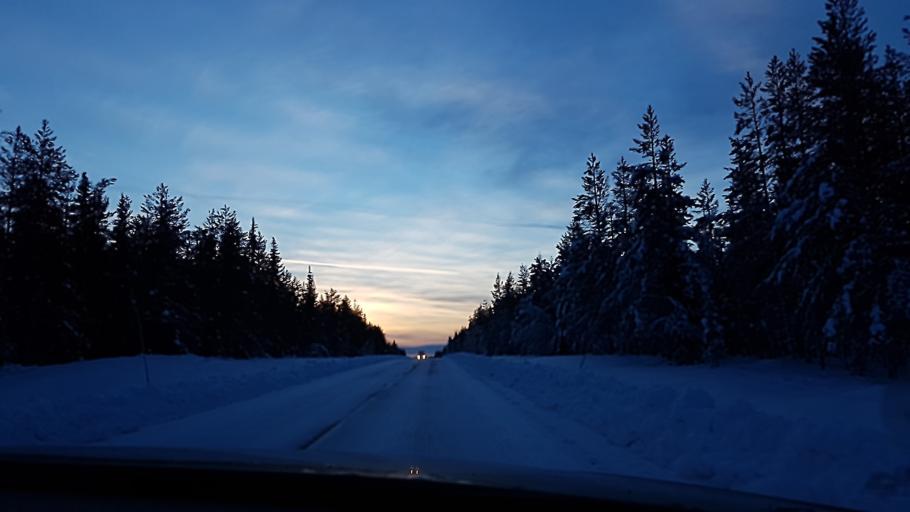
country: SE
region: Norrbotten
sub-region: Jokkmokks Kommun
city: Jokkmokk
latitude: 66.0910
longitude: 20.0706
